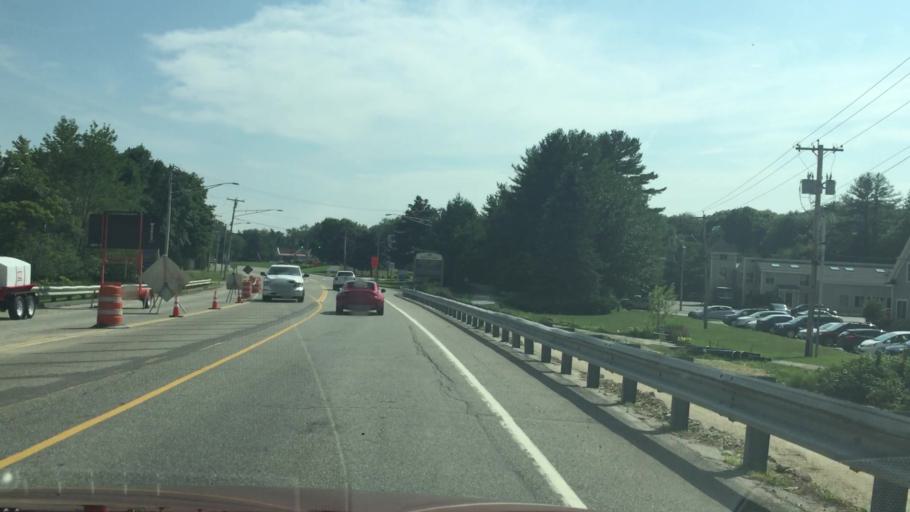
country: US
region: Maine
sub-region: Cumberland County
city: Yarmouth
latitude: 43.7995
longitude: -70.1877
